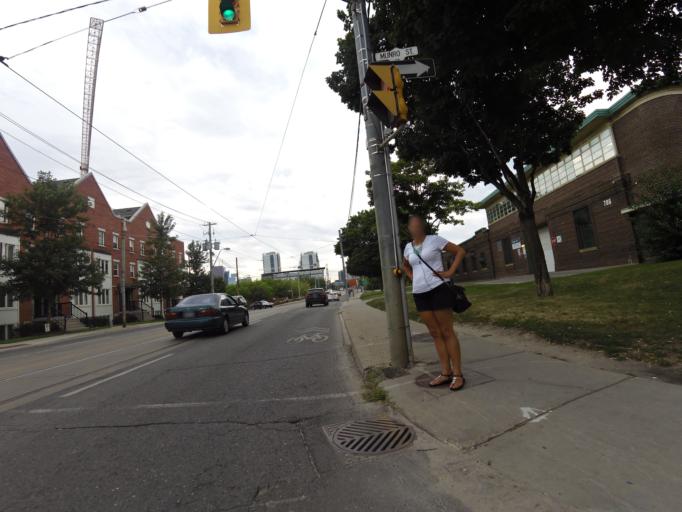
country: CA
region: Ontario
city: Toronto
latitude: 43.6621
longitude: -79.3530
